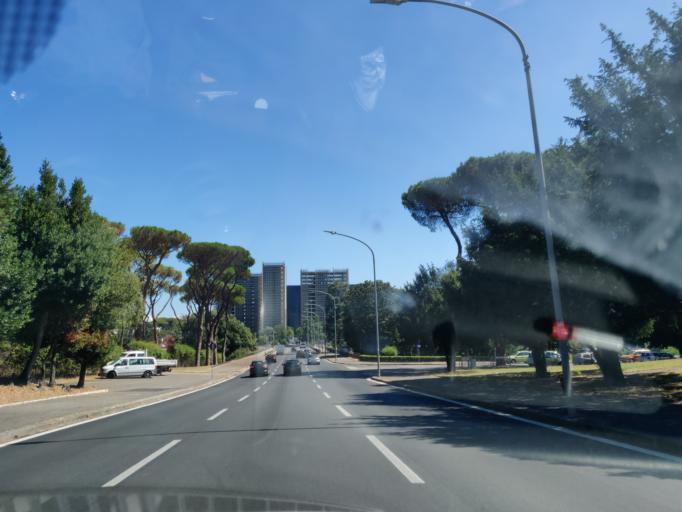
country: IT
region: Latium
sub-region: Citta metropolitana di Roma Capitale
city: Selcetta
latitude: 41.8259
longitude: 12.4687
